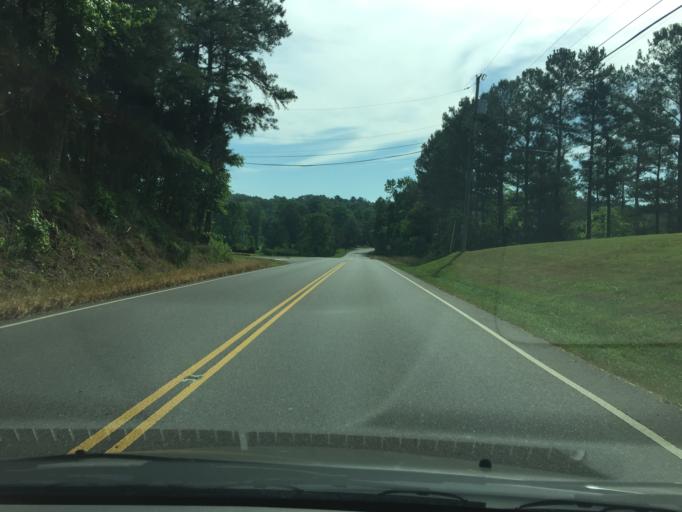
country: US
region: Tennessee
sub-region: Hamilton County
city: Collegedale
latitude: 35.1138
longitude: -84.9773
